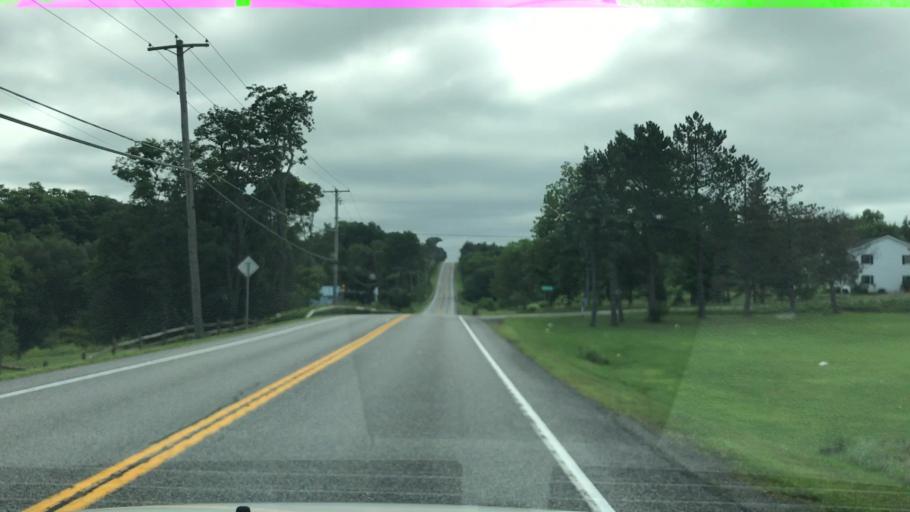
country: US
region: New York
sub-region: Wyoming County
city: Attica
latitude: 42.8360
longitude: -78.3761
